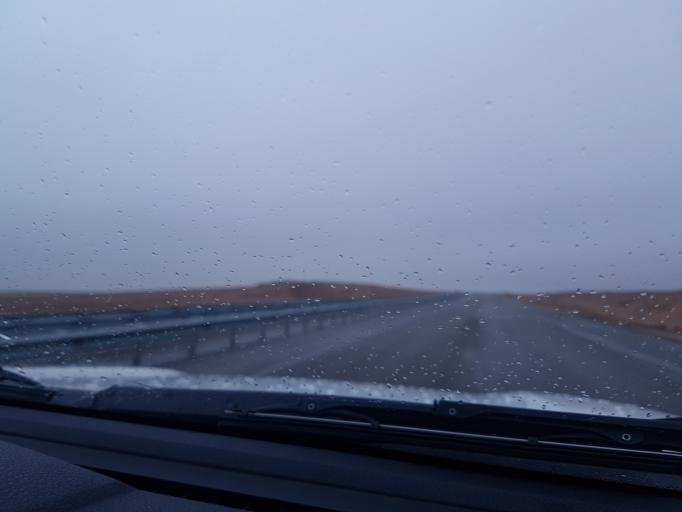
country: TM
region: Balkan
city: Balkanabat
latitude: 39.9693
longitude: 53.8027
